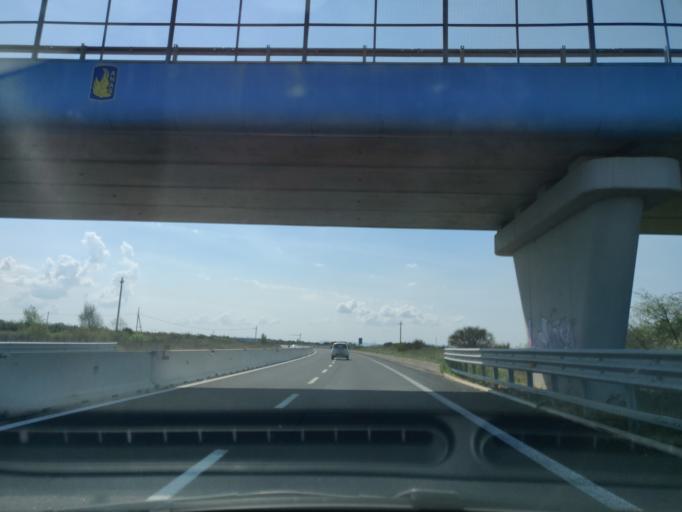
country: IT
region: Latium
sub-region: Provincia di Viterbo
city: Blera
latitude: 42.3515
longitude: 11.9812
